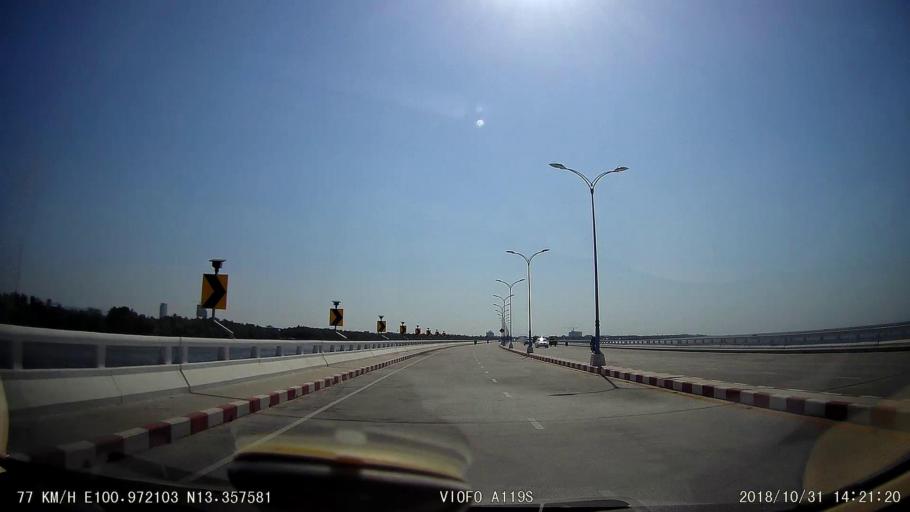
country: TH
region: Chon Buri
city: Chon Buri
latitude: 13.3575
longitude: 100.9720
